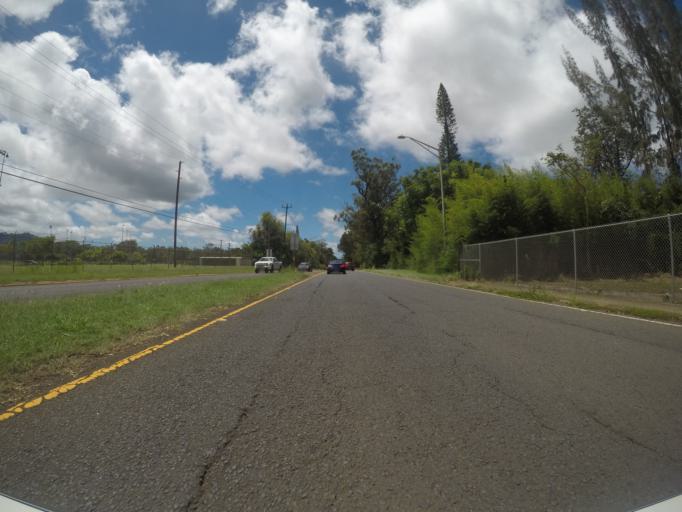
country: US
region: Hawaii
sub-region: Honolulu County
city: Schofield Barracks
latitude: 21.4965
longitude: -158.0509
